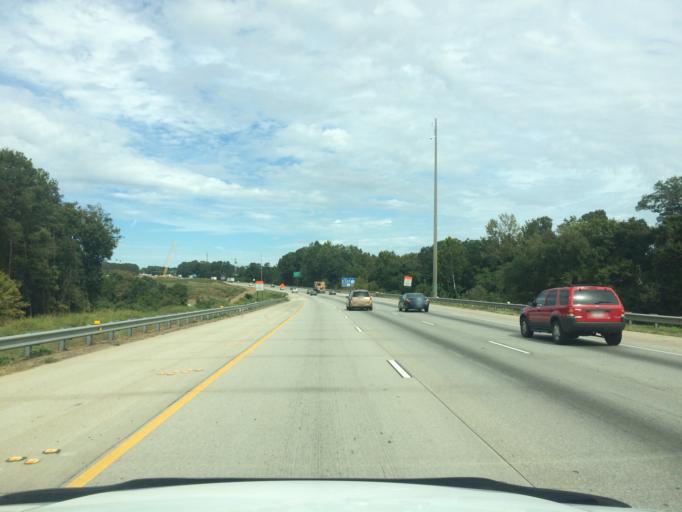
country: US
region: Georgia
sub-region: Cobb County
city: Kennesaw
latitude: 34.0197
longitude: -84.5700
